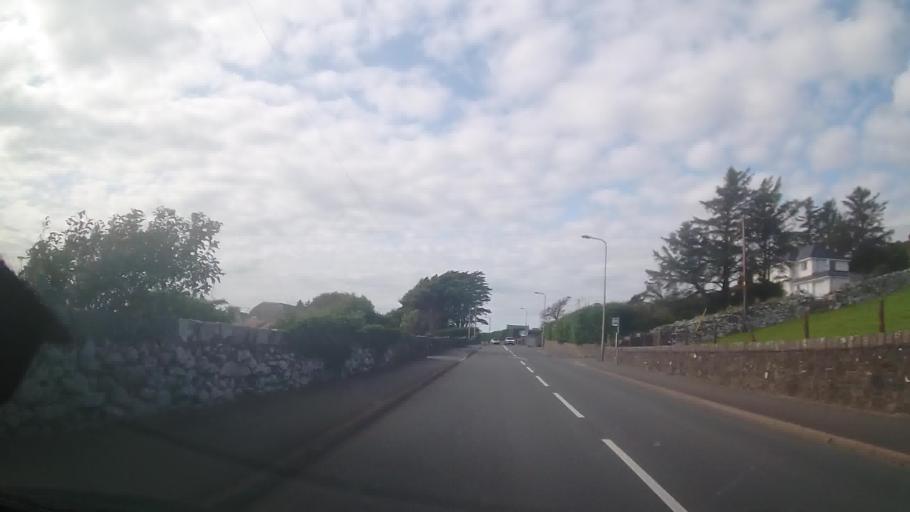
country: GB
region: Wales
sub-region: Gwynedd
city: Barmouth
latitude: 52.7383
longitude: -4.0722
